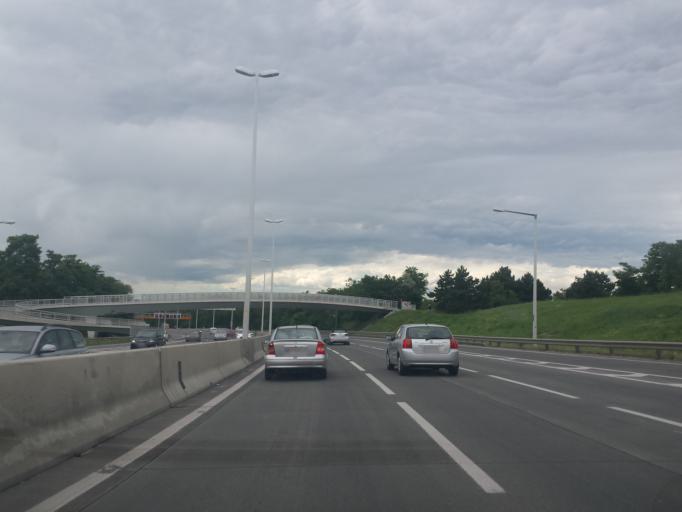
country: AT
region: Lower Austria
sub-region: Politischer Bezirk Wien-Umgebung
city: Leopoldsdorf
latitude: 48.1573
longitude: 16.3758
